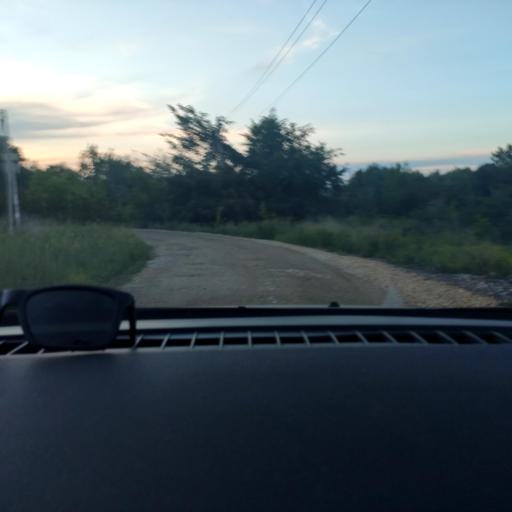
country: RU
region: Samara
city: Dubovyy Umet
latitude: 53.0373
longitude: 50.1730
